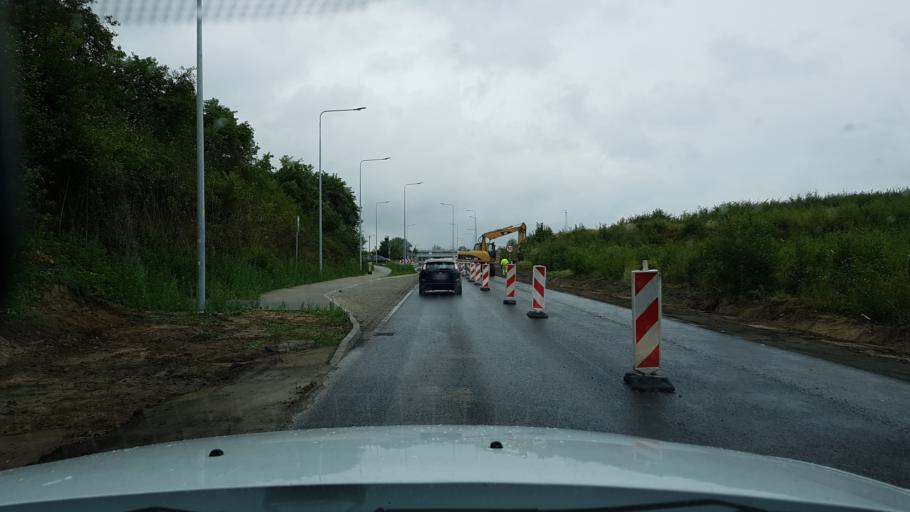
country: PL
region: West Pomeranian Voivodeship
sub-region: Powiat goleniowski
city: Maszewo
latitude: 53.4360
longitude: 15.0738
